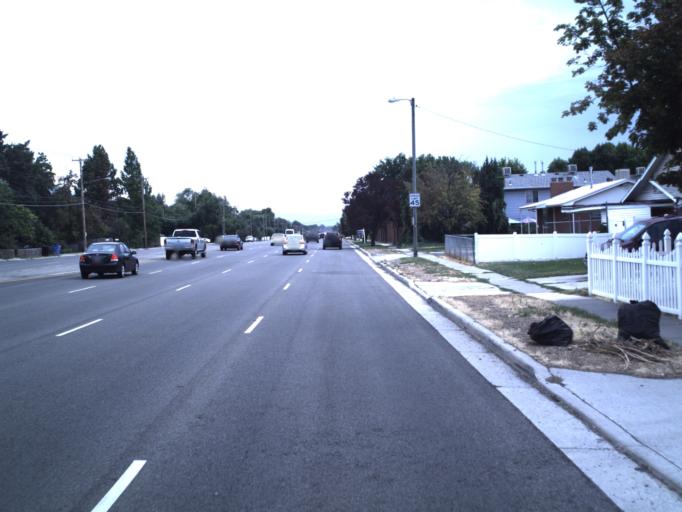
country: US
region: Utah
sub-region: Salt Lake County
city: South Salt Lake
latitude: 40.7079
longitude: -111.8715
